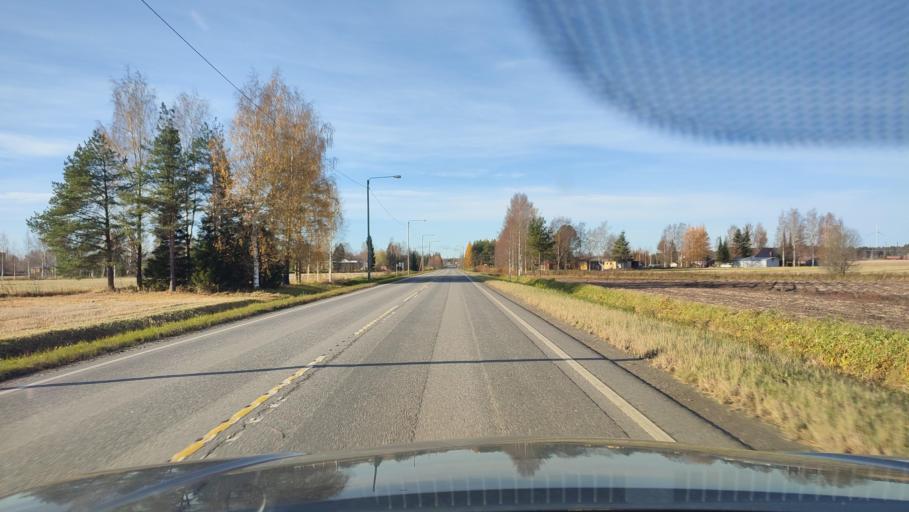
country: FI
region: Southern Ostrobothnia
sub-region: Suupohja
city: Teuva
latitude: 62.4919
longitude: 21.7681
